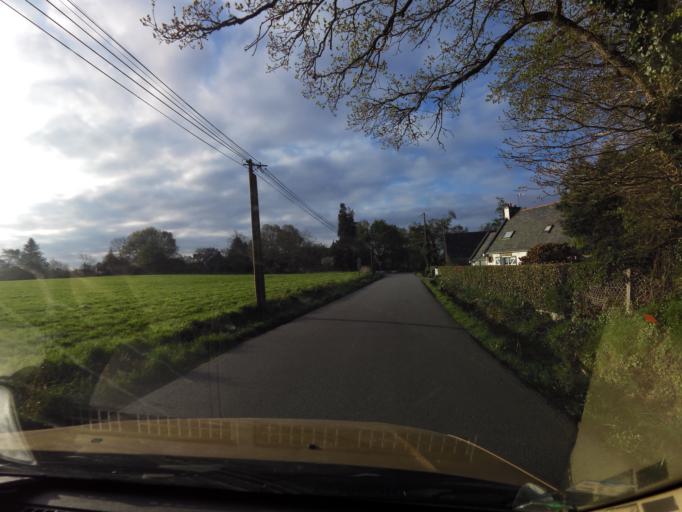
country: FR
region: Brittany
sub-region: Departement du Morbihan
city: Arradon
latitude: 47.6335
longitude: -2.8137
